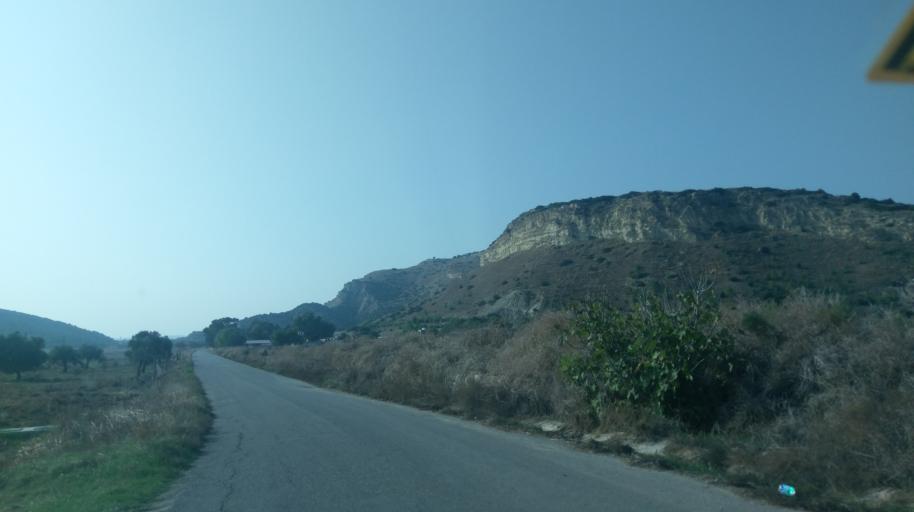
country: CY
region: Ammochostos
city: Rizokarpaso
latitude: 35.5159
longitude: 34.3032
